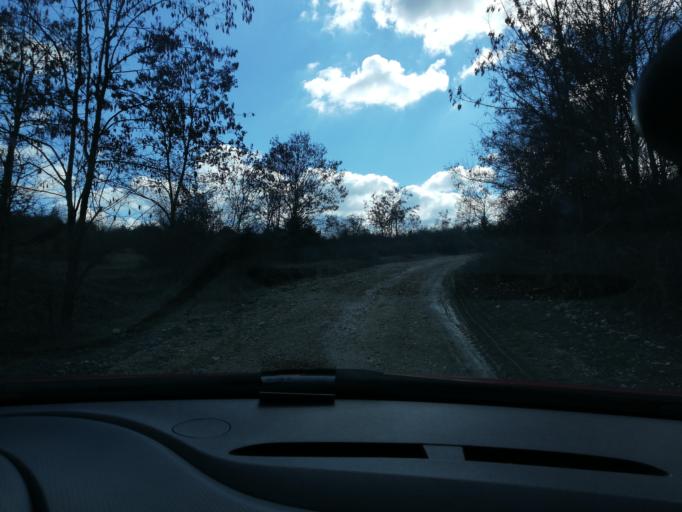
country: TR
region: Kastamonu
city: Igdir
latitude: 41.2274
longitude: 33.0266
